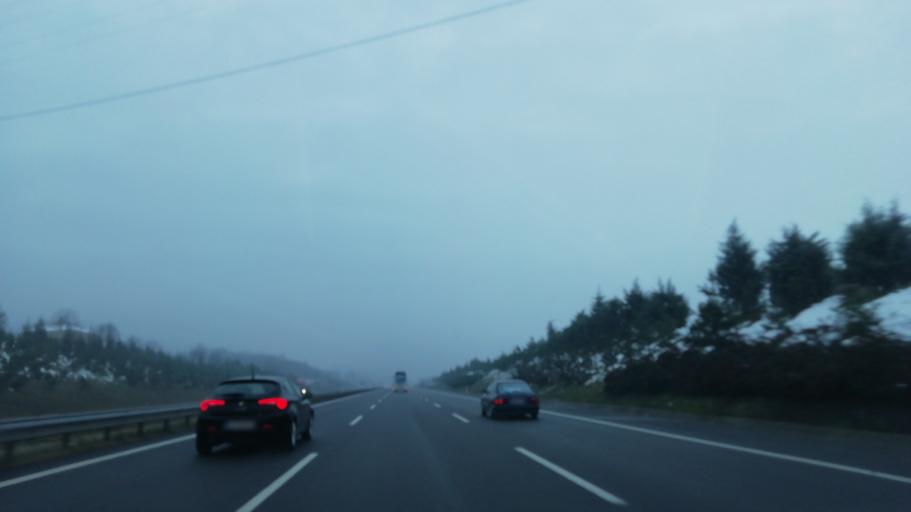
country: TR
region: Duzce
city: Kaynasli
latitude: 40.7801
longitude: 31.3437
